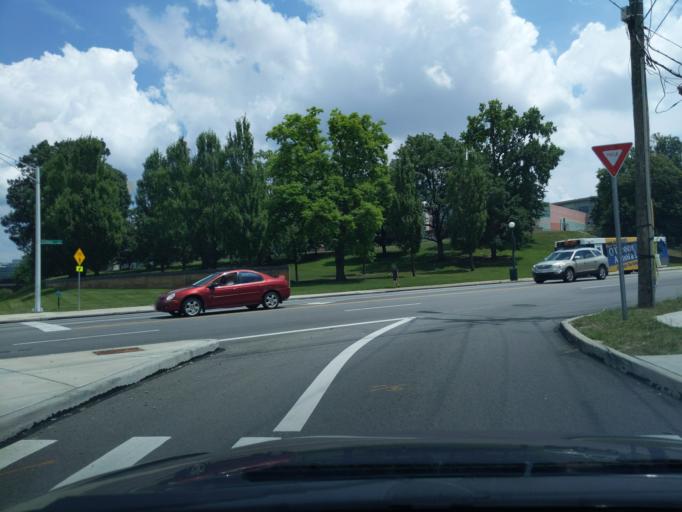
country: US
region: Ohio
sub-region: Hamilton County
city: Saint Bernard
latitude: 39.1353
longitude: -84.5203
